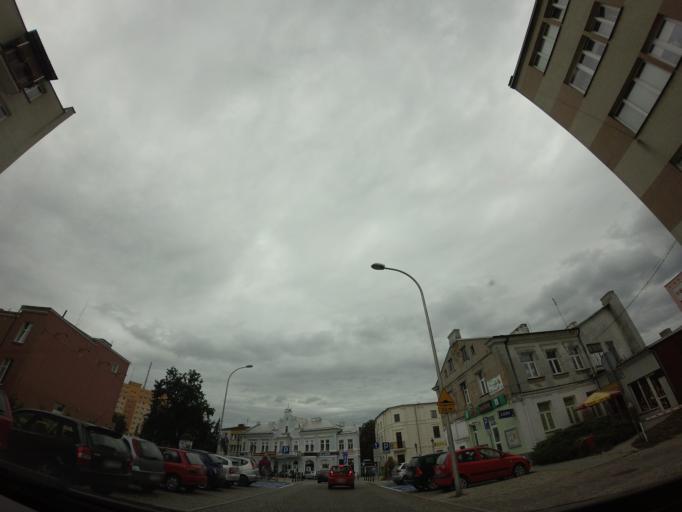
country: PL
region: Masovian Voivodeship
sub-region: Powiat ciechanowski
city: Ciechanow
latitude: 52.8789
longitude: 20.6185
